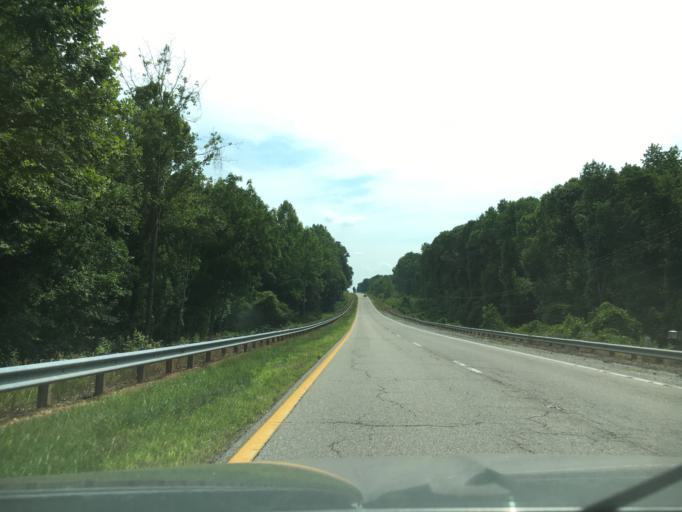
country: US
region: Virginia
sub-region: Nottoway County
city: Crewe
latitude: 37.1587
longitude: -78.2697
